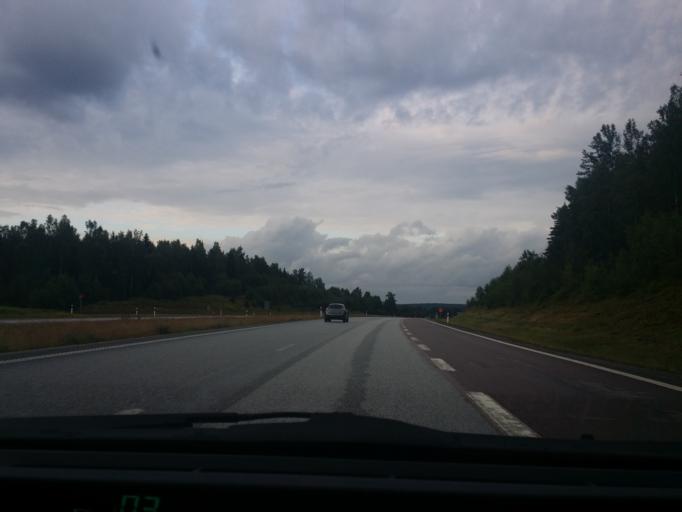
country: SE
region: Vaestmanland
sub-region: Kopings Kommun
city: Koping
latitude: 59.5126
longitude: 15.9465
